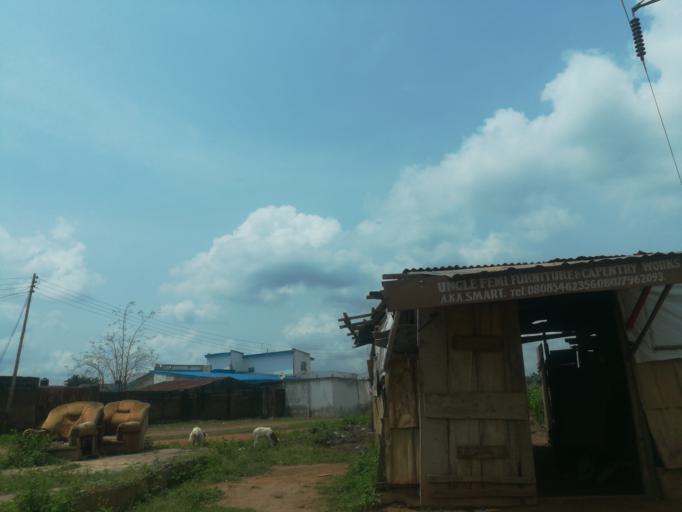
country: NG
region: Oyo
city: Moniya
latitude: 7.4549
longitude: 3.9573
